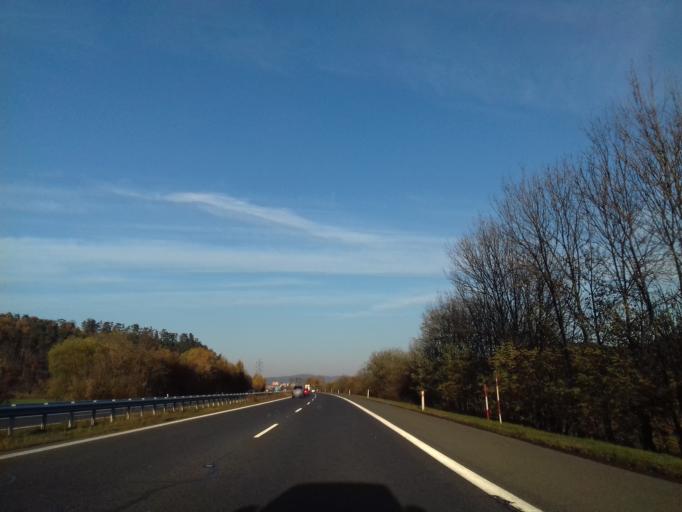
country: CZ
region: Central Bohemia
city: Zdice
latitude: 49.9210
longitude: 14.0050
